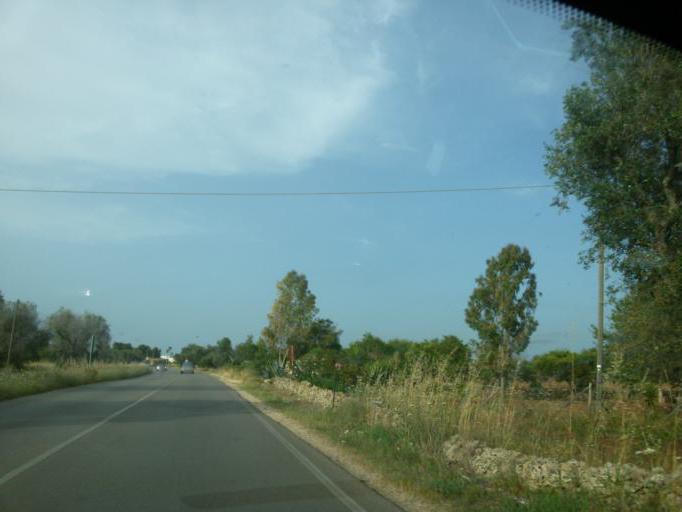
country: IT
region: Apulia
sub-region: Provincia di Brindisi
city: San Pietro Vernotico
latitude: 40.4817
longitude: 17.9846
